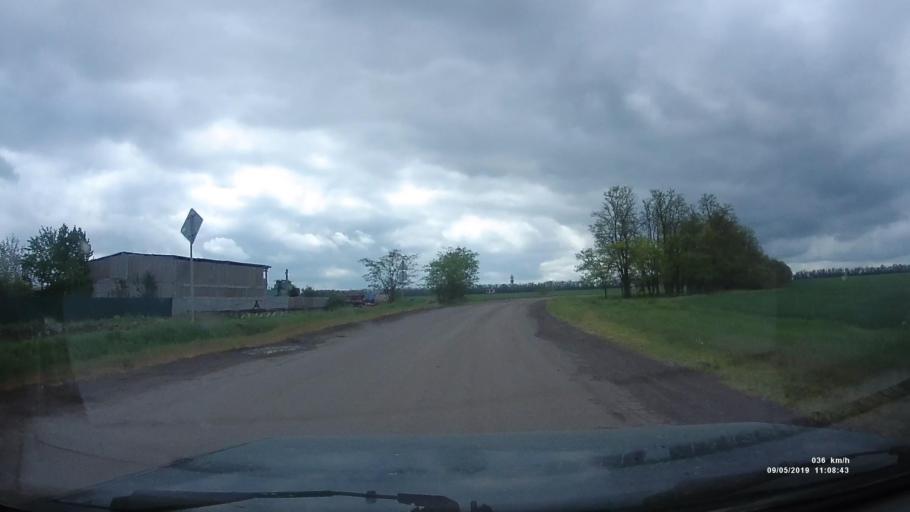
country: RU
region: Krasnodarskiy
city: Kanelovskaya
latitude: 46.7882
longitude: 39.2112
